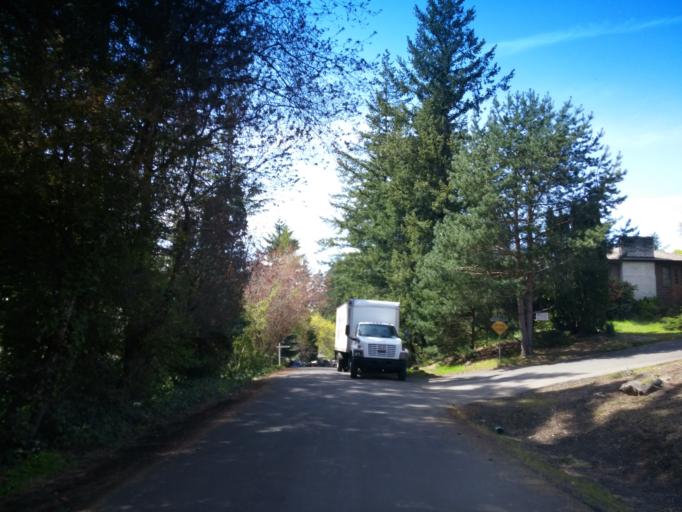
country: US
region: Oregon
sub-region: Washington County
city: Cedar Mill
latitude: 45.5332
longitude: -122.7957
